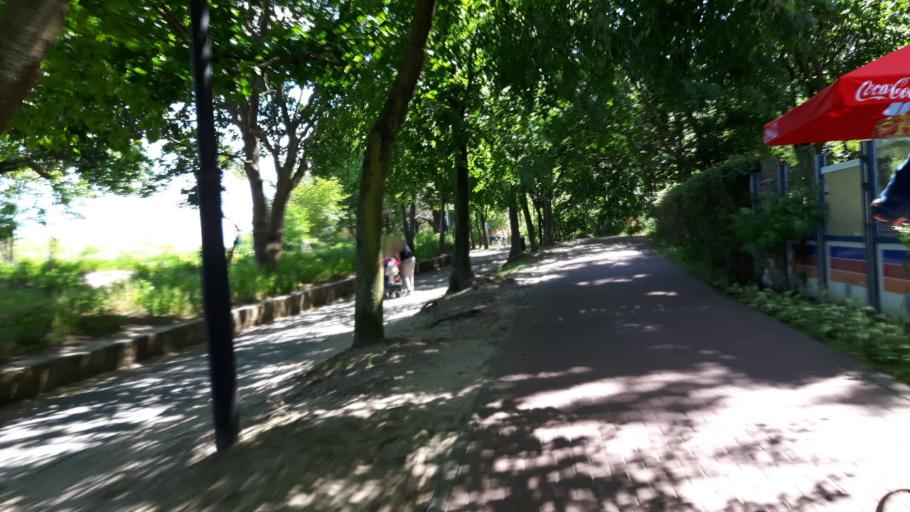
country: PL
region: Pomeranian Voivodeship
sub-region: Sopot
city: Sopot
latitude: 54.4315
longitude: 18.5881
